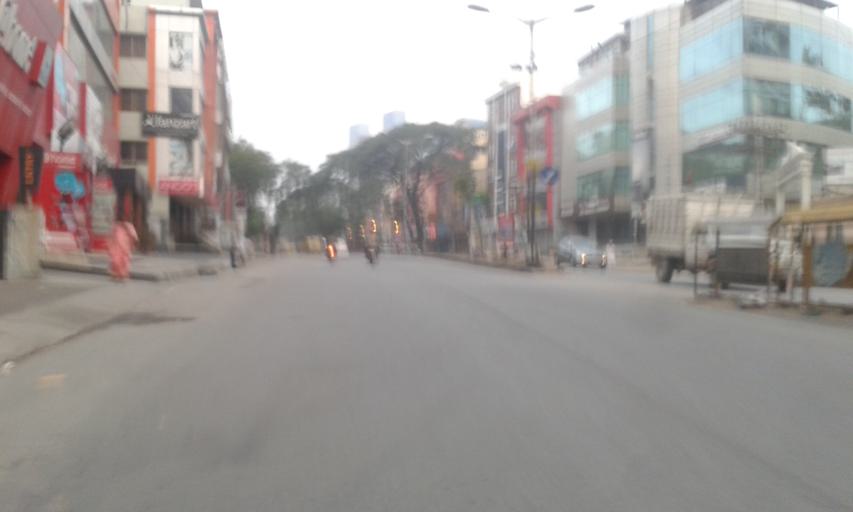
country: IN
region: Karnataka
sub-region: Bangalore Urban
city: Bangalore
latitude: 12.9347
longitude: 77.6097
